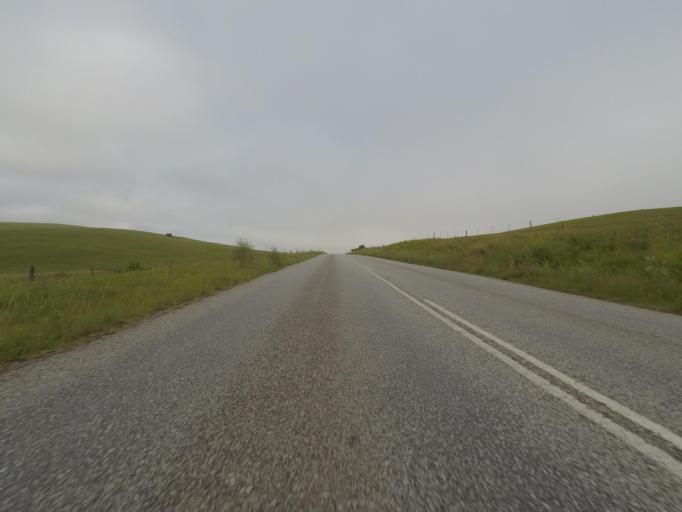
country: ZA
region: Eastern Cape
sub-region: Cacadu District Municipality
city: Port Alfred
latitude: -33.6080
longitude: 26.8179
